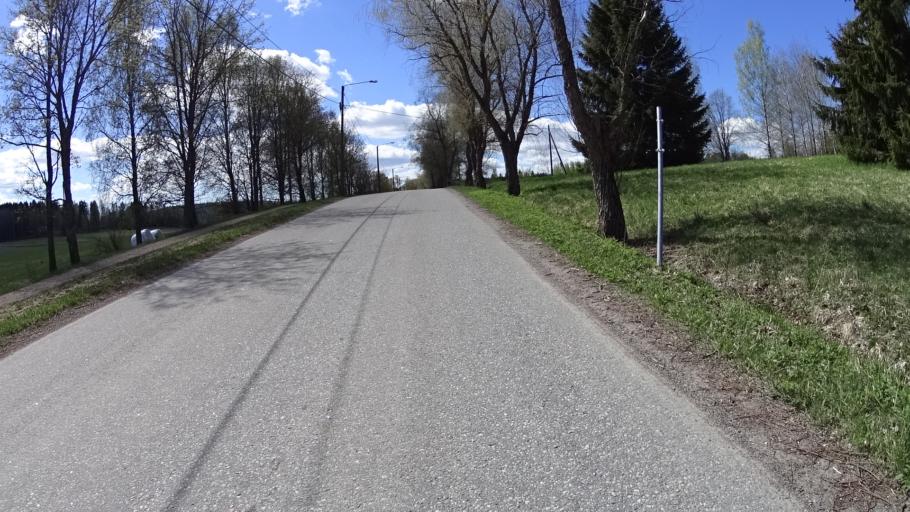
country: FI
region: Uusimaa
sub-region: Helsinki
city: Vihti
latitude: 60.3774
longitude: 24.5095
